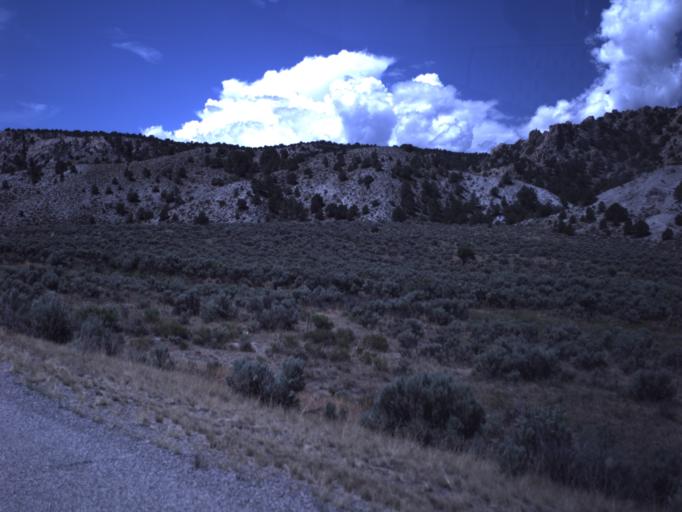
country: US
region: Utah
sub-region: Piute County
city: Junction
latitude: 38.0511
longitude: -112.3533
